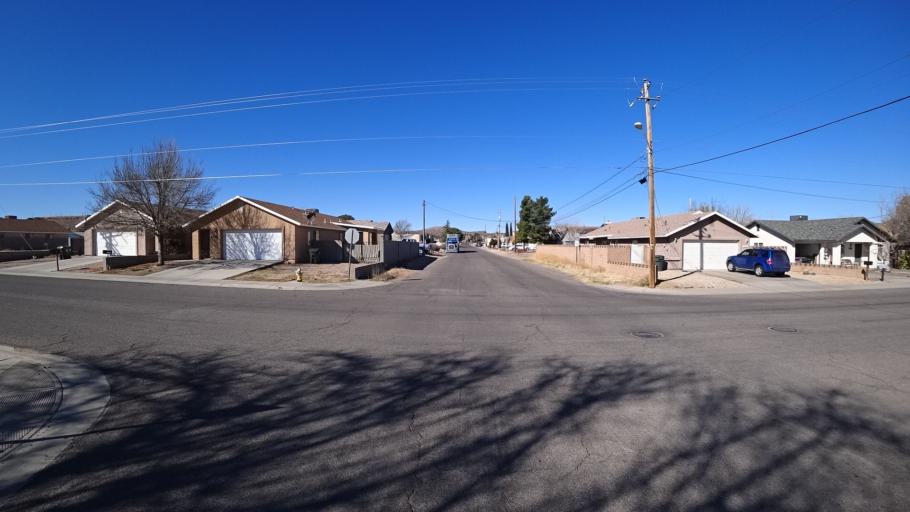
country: US
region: Arizona
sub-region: Mohave County
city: Kingman
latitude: 35.2075
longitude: -114.0313
